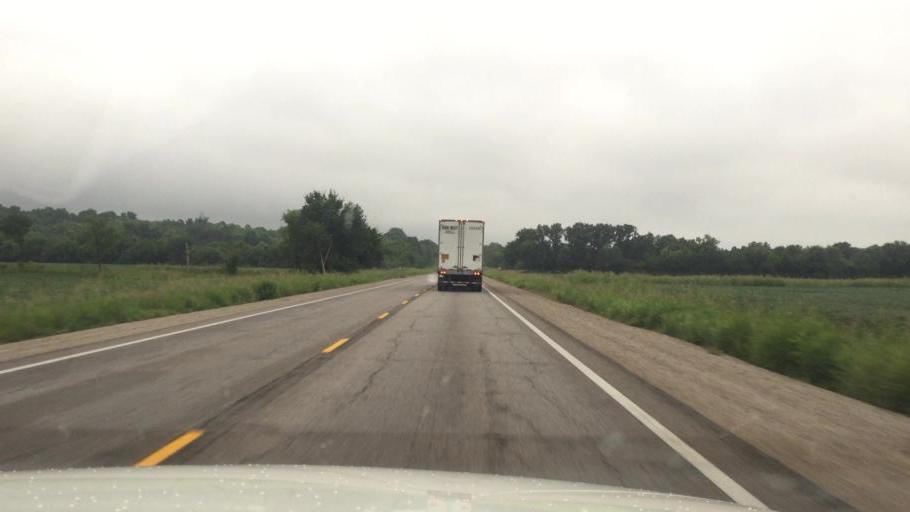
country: US
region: Kansas
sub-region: Montgomery County
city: Cherryvale
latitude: 37.1685
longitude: -95.5766
